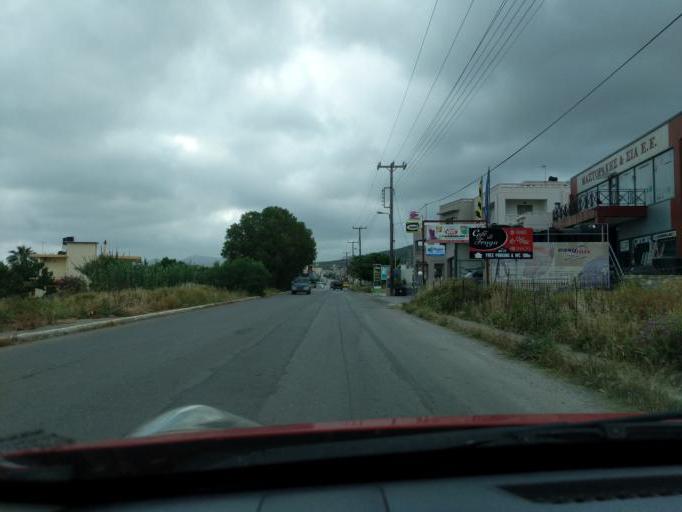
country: GR
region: Crete
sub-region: Nomos Chanias
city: Kissamos
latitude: 35.4988
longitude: 23.6458
